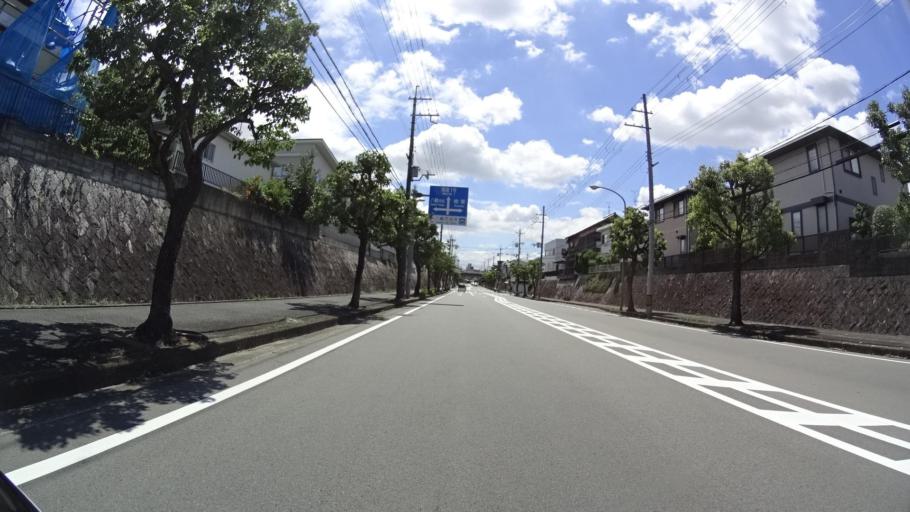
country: JP
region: Kyoto
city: Yawata
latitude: 34.8722
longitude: 135.6891
